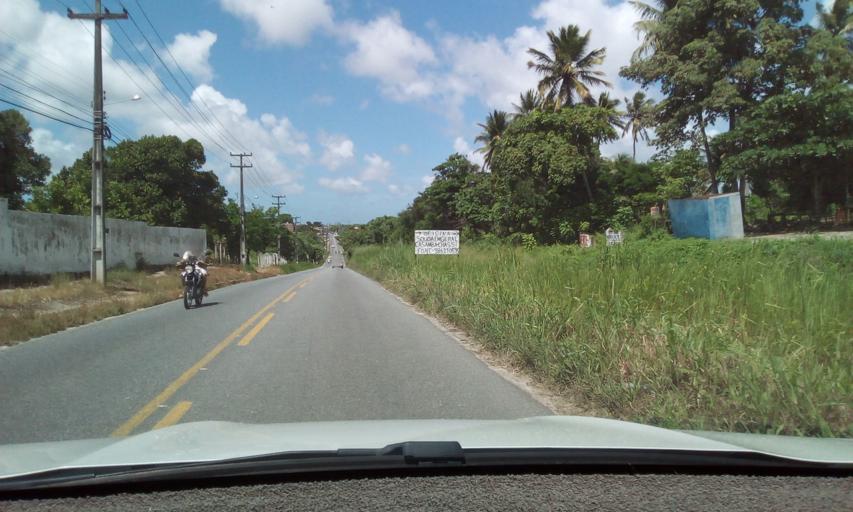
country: BR
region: Paraiba
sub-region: Bayeux
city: Bayeux
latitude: -7.1227
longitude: -34.9354
